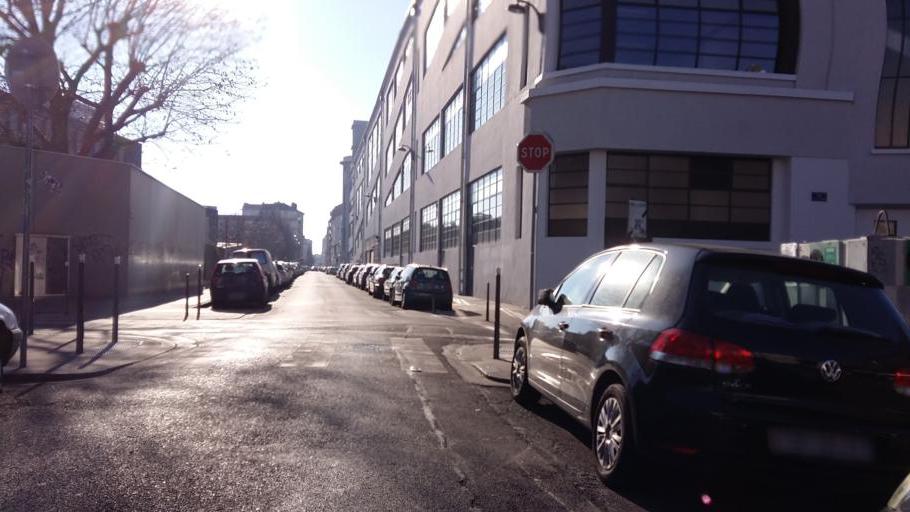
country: FR
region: Rhone-Alpes
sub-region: Departement du Rhone
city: Lyon
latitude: 45.7517
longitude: 4.8412
